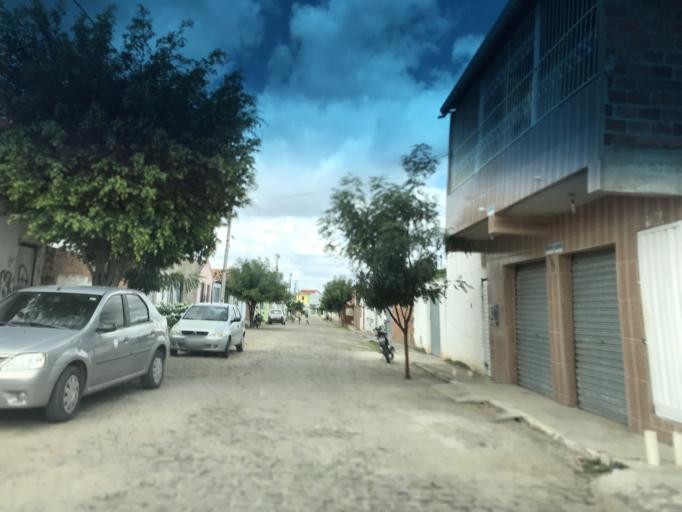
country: BR
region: Bahia
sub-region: Itaberaba
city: Itaberaba
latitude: -12.5358
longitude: -40.3036
